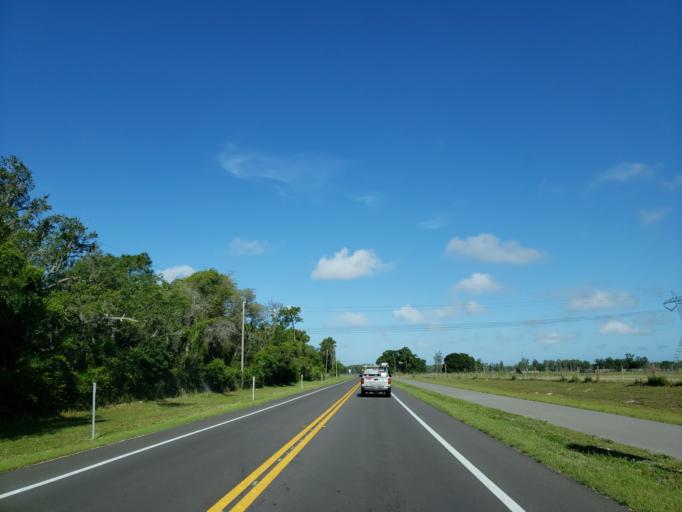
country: US
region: Florida
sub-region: Hillsborough County
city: Keystone
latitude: 28.1451
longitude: -82.6512
